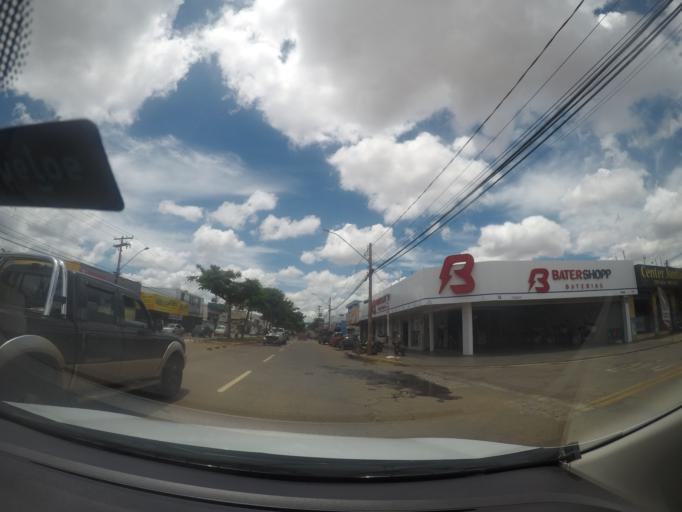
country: BR
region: Goias
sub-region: Goiania
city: Goiania
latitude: -16.6707
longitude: -49.3092
